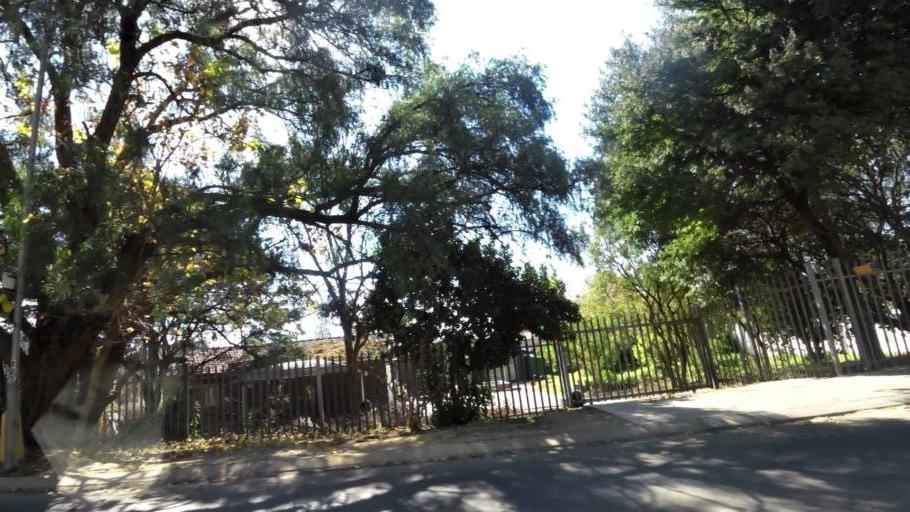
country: ZA
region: Gauteng
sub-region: City of Johannesburg Metropolitan Municipality
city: Roodepoort
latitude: -26.1431
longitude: 27.9451
